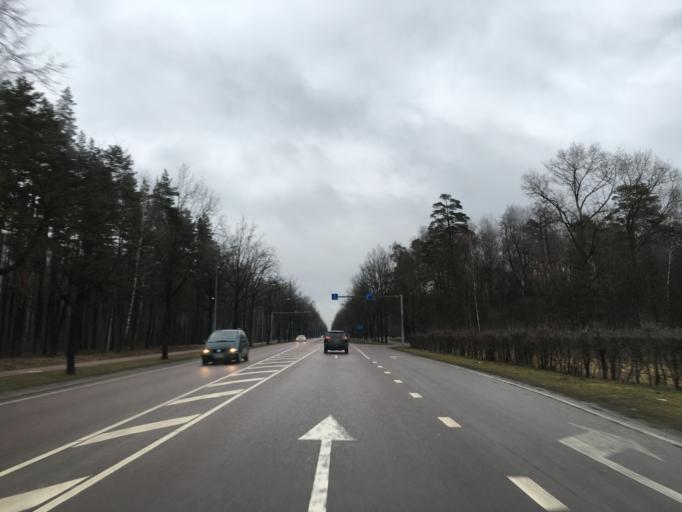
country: LV
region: Ozolnieku
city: Ozolnieki
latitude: 56.6739
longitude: 23.7688
